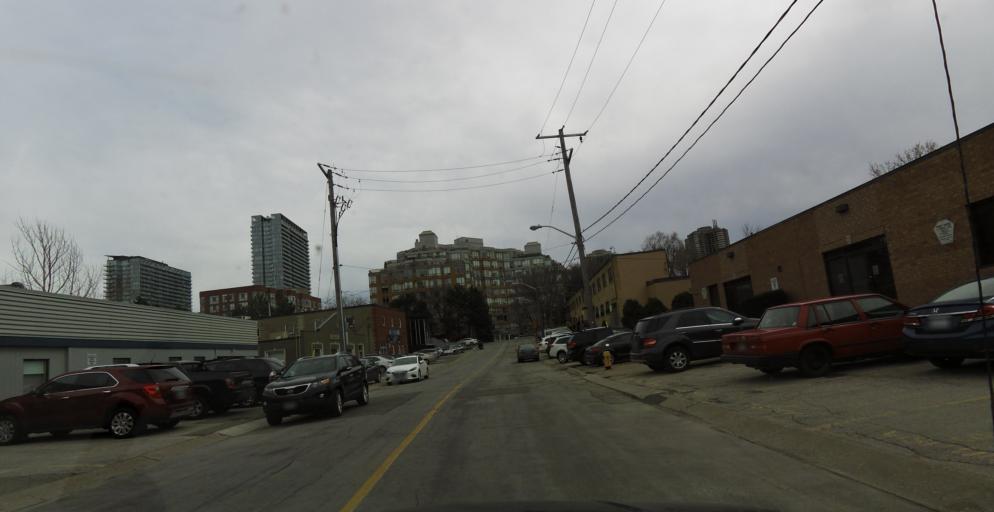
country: CA
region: Ontario
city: Toronto
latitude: 43.6380
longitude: -79.4751
